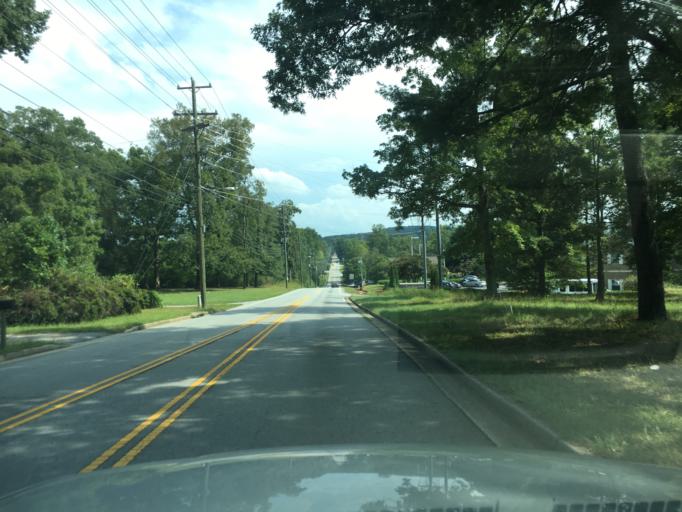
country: US
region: South Carolina
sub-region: Greenville County
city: Wade Hampton
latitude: 34.8540
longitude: -82.3205
